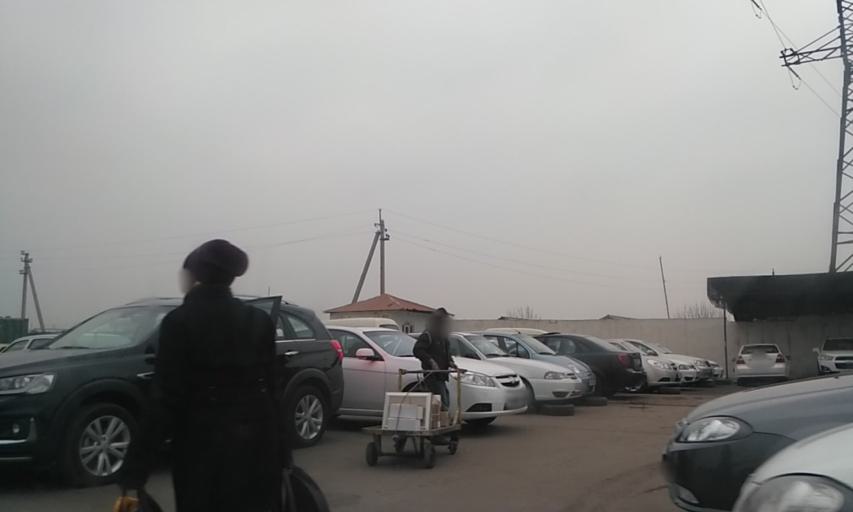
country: UZ
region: Toshkent Shahri
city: Tashkent
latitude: 41.2896
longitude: 69.1501
